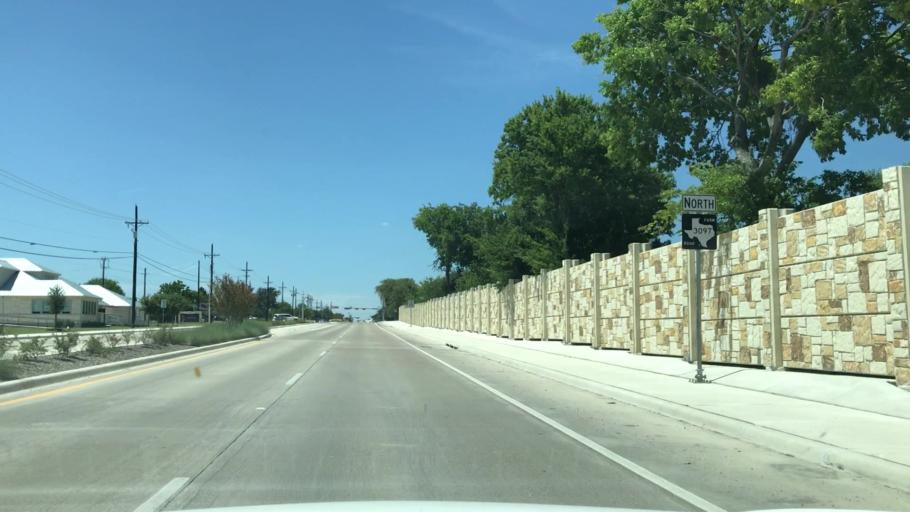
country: US
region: Texas
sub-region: Rockwall County
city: Rockwall
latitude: 32.8871
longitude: -96.4658
